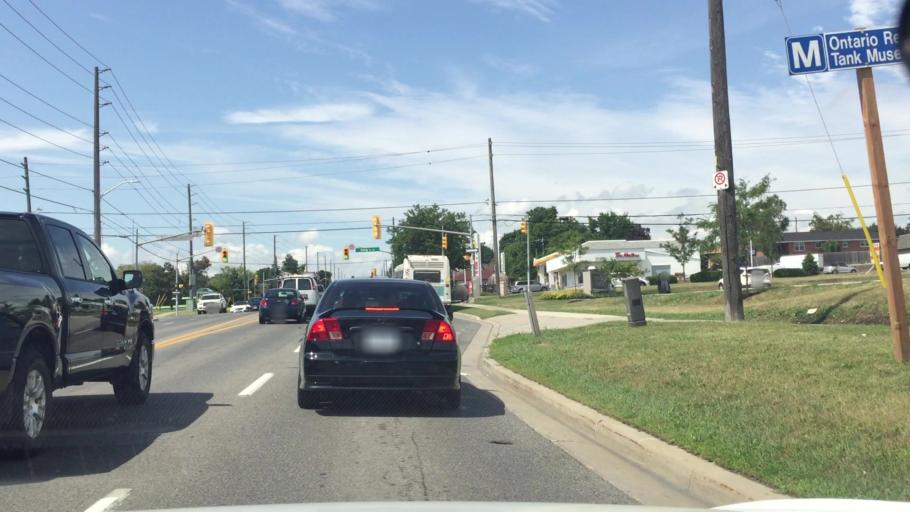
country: CA
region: Ontario
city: Oshawa
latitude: 43.8925
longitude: -78.8830
